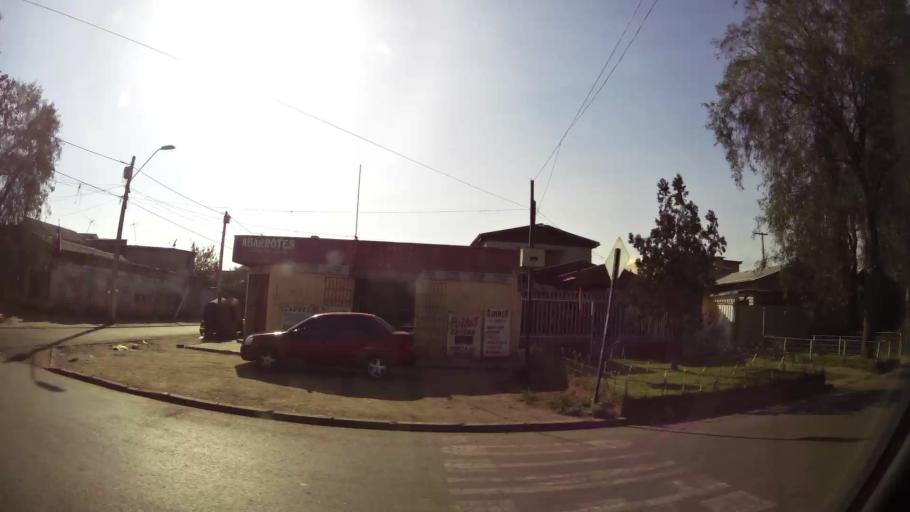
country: CL
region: Santiago Metropolitan
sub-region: Provincia de Santiago
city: Lo Prado
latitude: -33.4186
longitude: -70.7474
